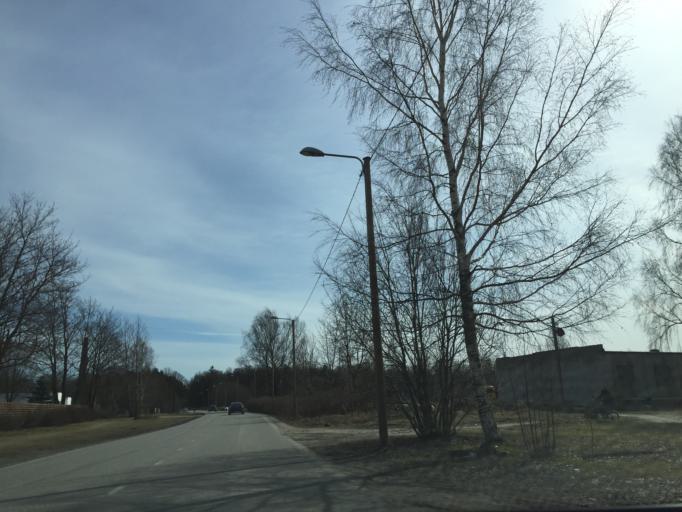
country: EE
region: Paernumaa
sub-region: Paernu linn
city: Parnu
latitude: 58.3808
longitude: 24.5313
